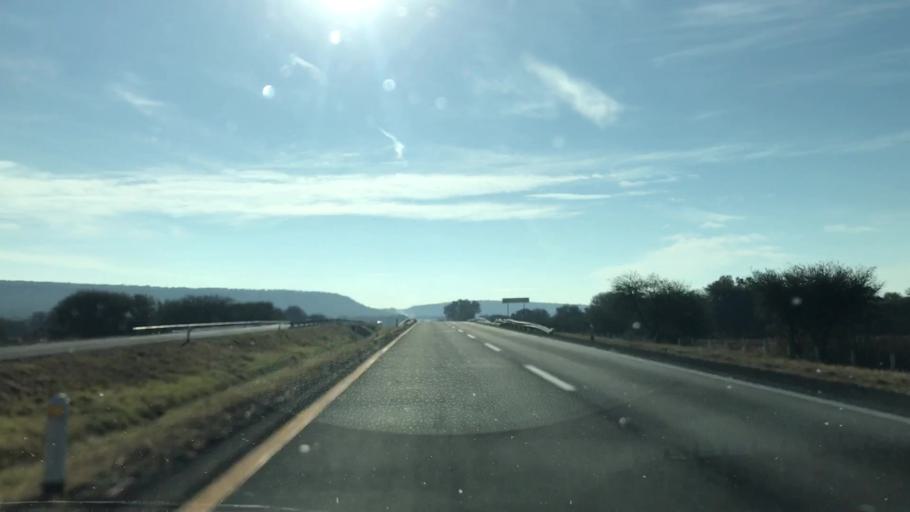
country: MX
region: Guanajuato
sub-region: Purisima del Rincon
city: Potrerillos (Guanajal)
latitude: 21.1563
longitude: -101.8518
